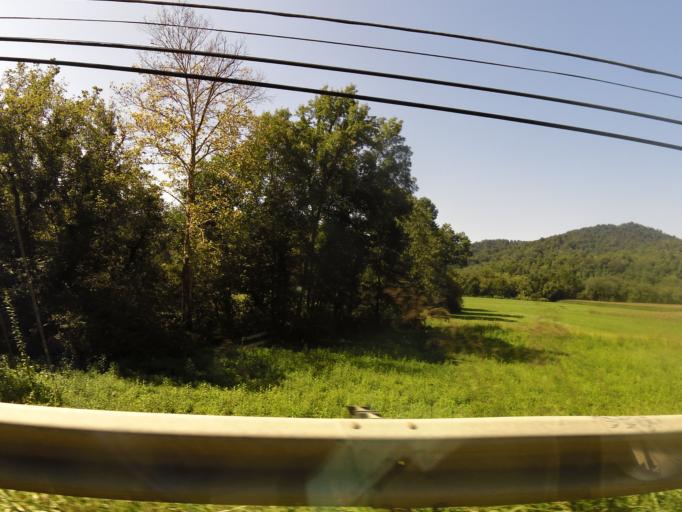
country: US
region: Kentucky
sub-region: Clay County
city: Manchester
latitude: 37.0899
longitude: -83.7028
